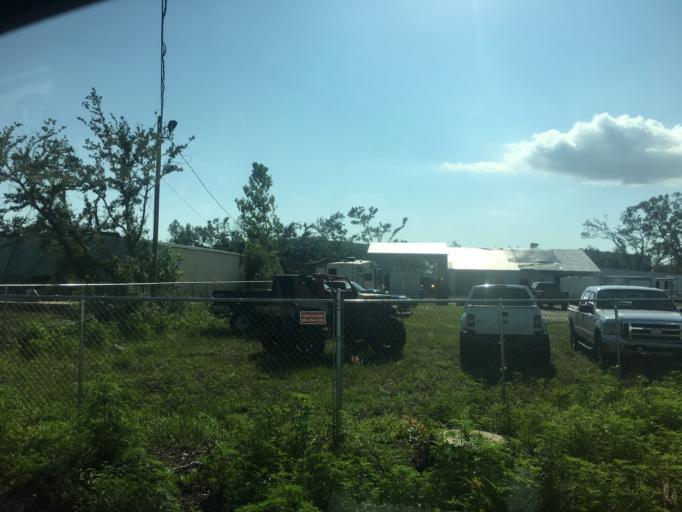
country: US
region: Florida
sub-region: Bay County
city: Cedar Grove
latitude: 30.1616
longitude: -85.6209
